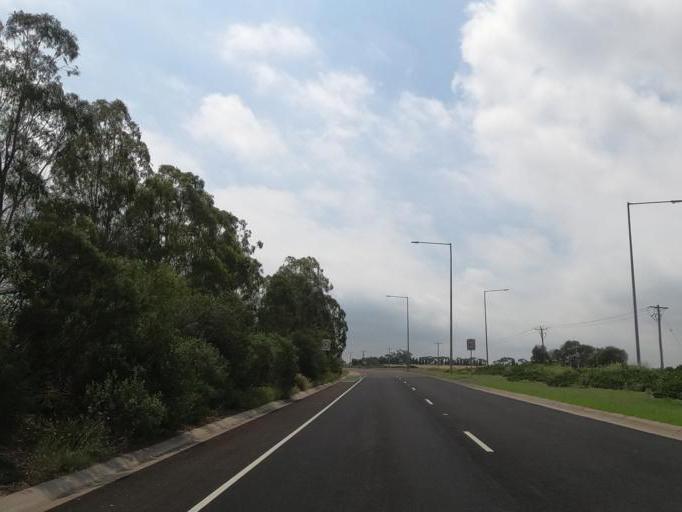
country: AU
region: Victoria
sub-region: Hume
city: Attwood
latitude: -37.6693
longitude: 144.8854
